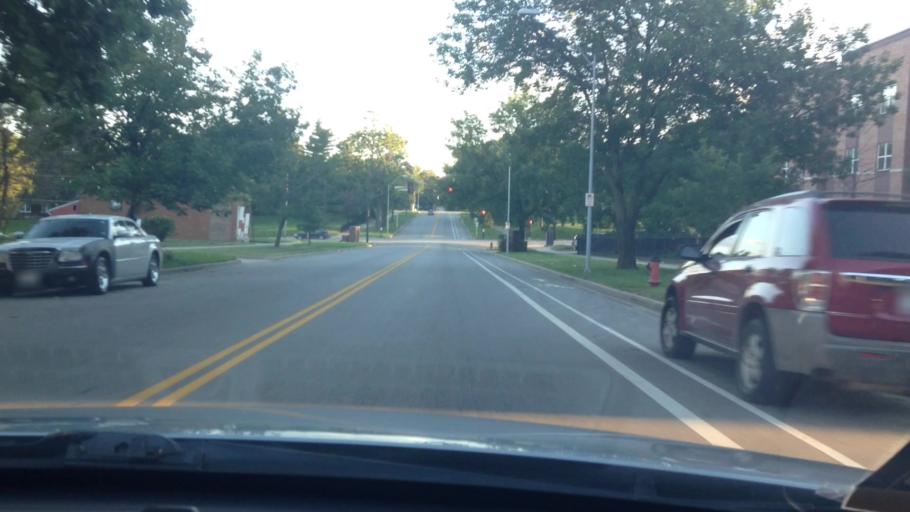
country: US
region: Missouri
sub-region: Jackson County
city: Kansas City
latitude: 39.0709
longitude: -94.5493
